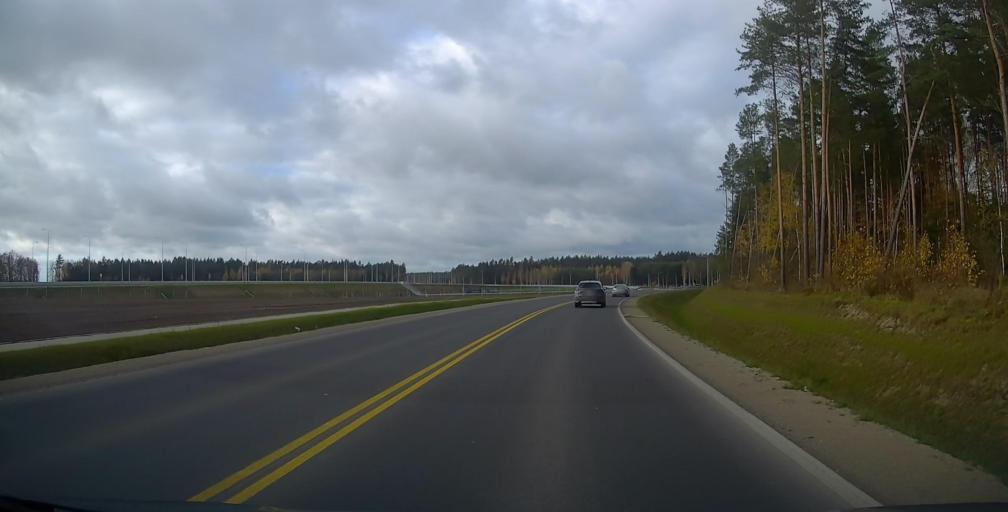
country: PL
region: Warmian-Masurian Voivodeship
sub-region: Powiat elcki
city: Elk
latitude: 53.8381
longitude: 22.4222
